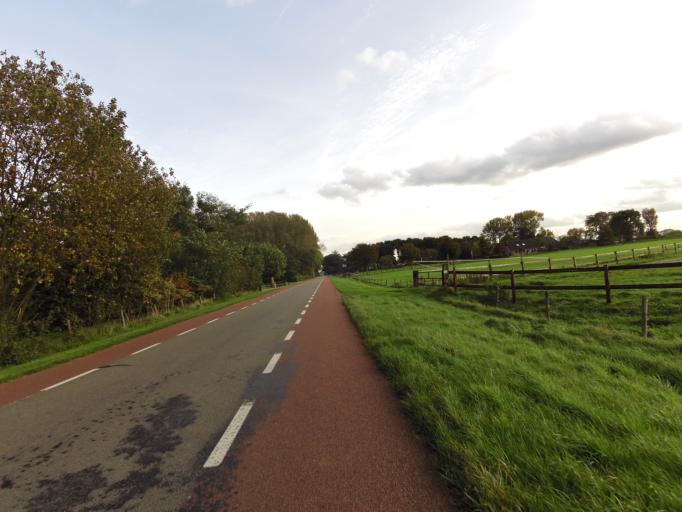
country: NL
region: Gelderland
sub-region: Gemeente Zutphen
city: Zutphen
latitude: 52.1173
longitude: 6.2042
